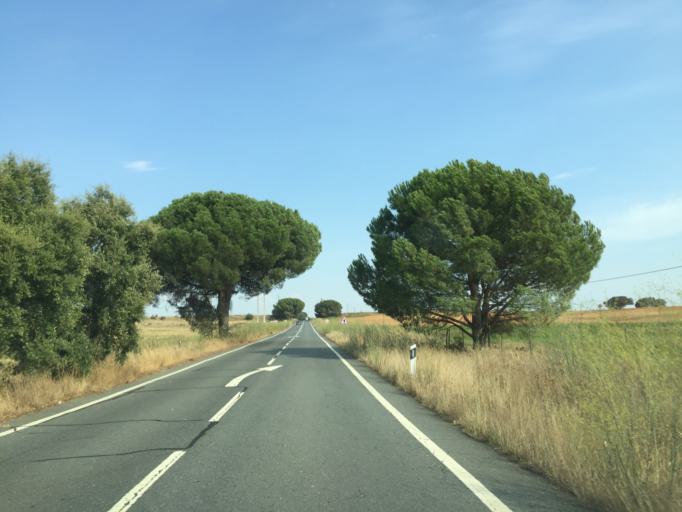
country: PT
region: Beja
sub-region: Aljustrel
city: Aljustrel
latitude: 37.9317
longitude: -8.3481
